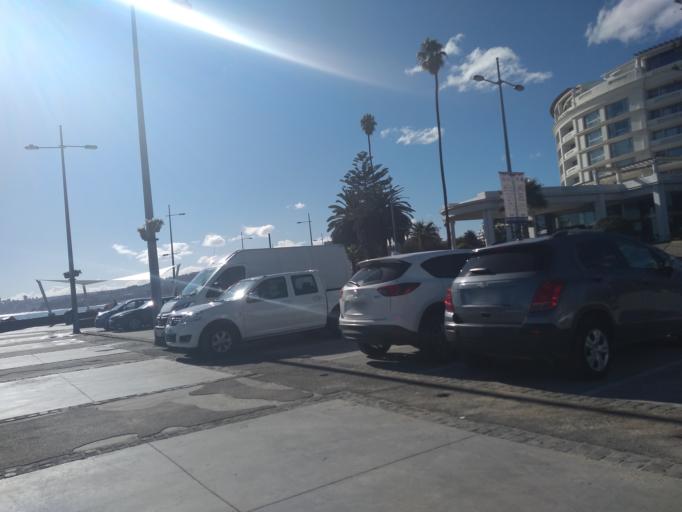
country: CL
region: Valparaiso
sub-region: Provincia de Valparaiso
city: Vina del Mar
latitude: -33.0188
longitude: -71.5618
